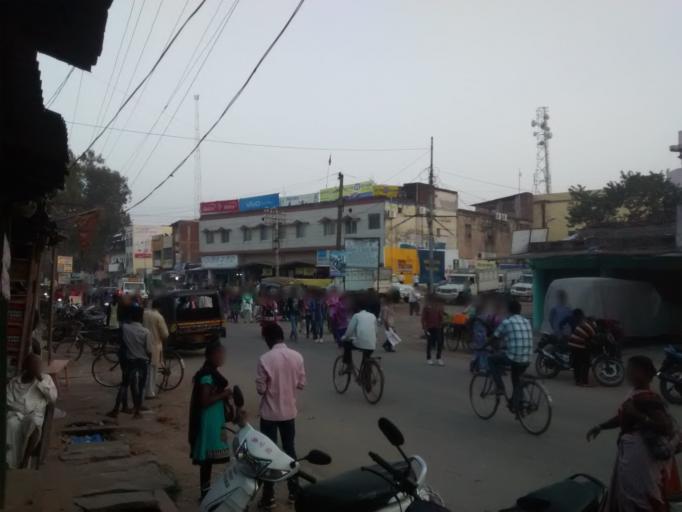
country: IN
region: Chhattisgarh
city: Gumla
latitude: 23.0412
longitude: 84.5448
